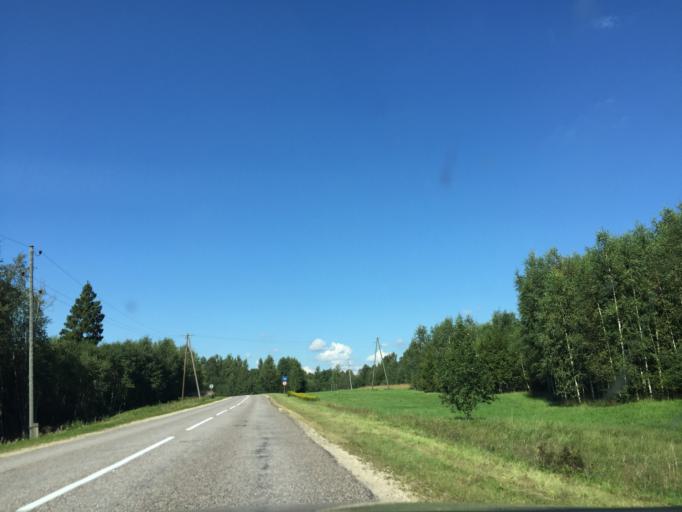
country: LV
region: Limbazu Rajons
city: Limbazi
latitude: 57.4715
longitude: 24.7120
